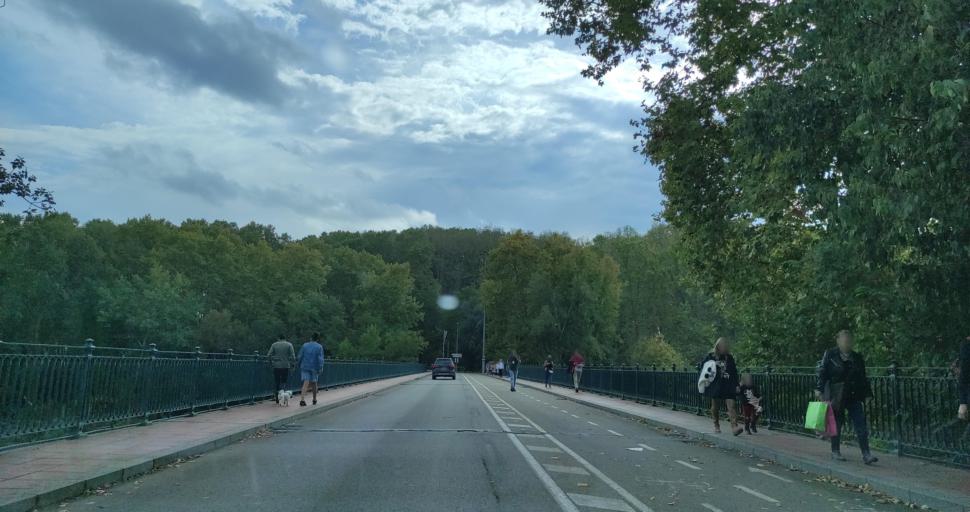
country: ES
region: Catalonia
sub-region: Provincia de Girona
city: Girona
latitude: 41.9910
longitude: 2.8188
